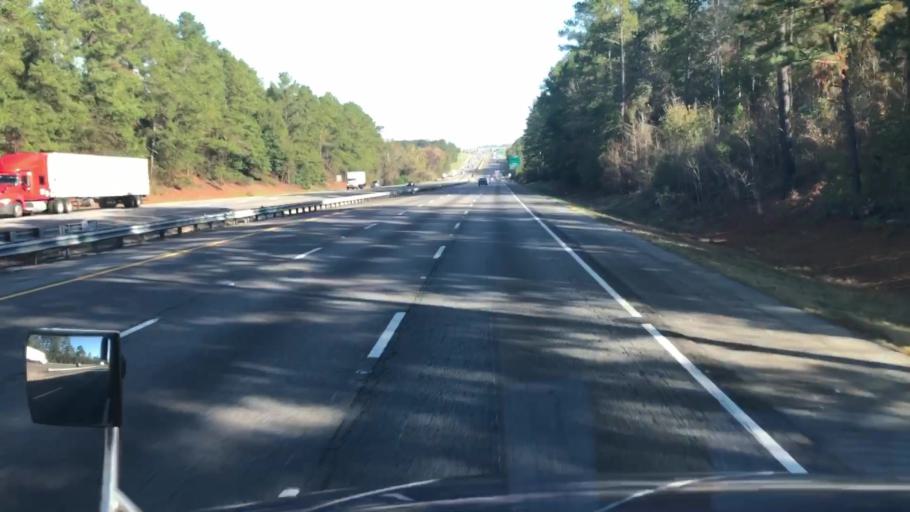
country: US
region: Georgia
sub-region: Houston County
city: Perry
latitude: 32.4146
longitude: -83.7624
